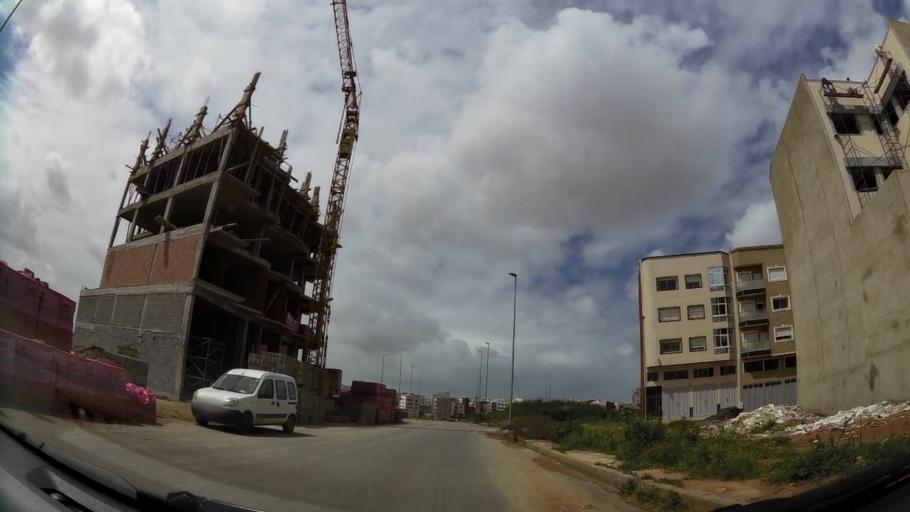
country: MA
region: Grand Casablanca
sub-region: Casablanca
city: Casablanca
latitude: 33.5280
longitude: -7.6031
